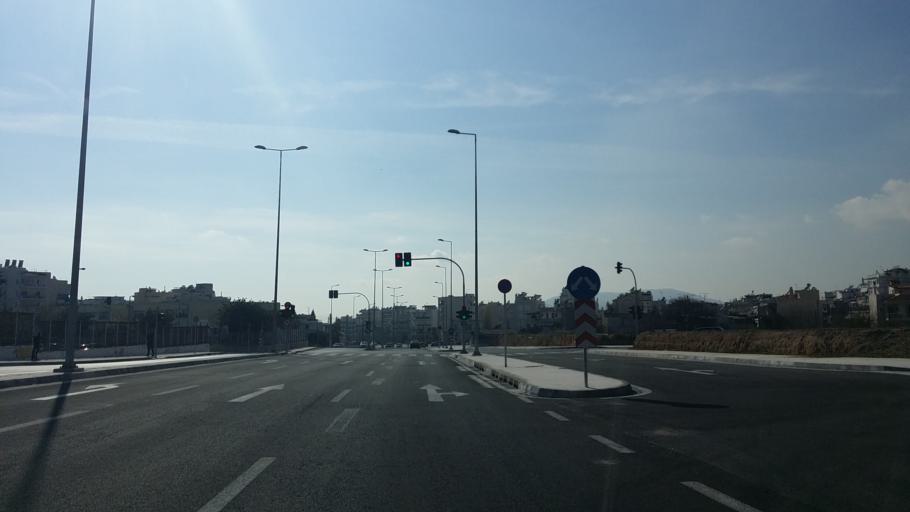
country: GR
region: Attica
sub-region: Nomarchia Athinas
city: Ilion
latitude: 38.0402
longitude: 23.7077
